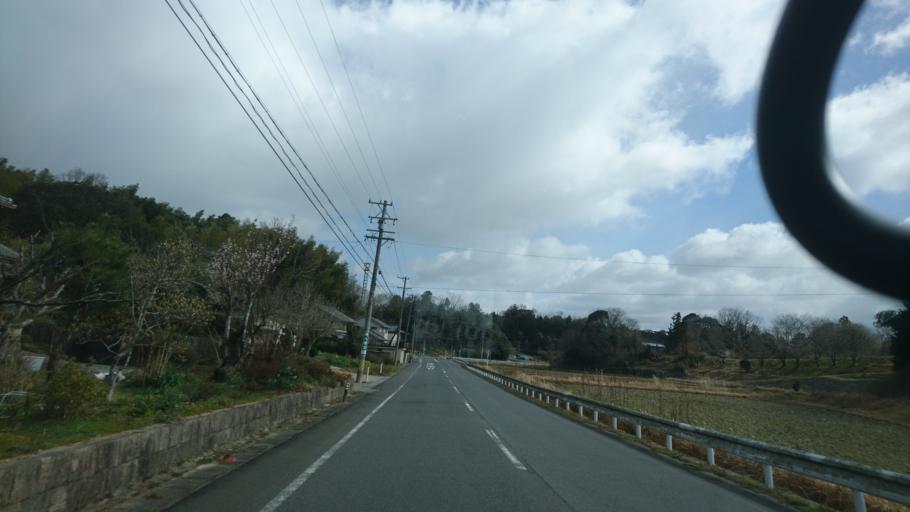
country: JP
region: Mie
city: Ueno-ebisumachi
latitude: 34.7277
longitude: 136.0723
